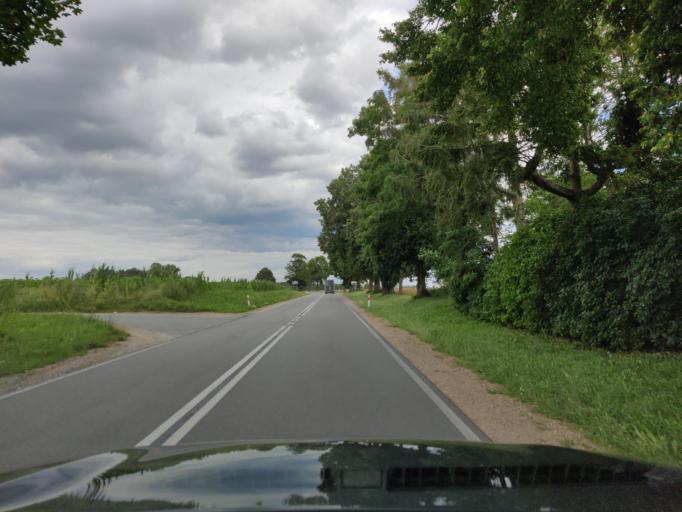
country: PL
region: Masovian Voivodeship
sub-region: Powiat sokolowski
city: Kosow Lacki
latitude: 52.5967
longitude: 22.1612
